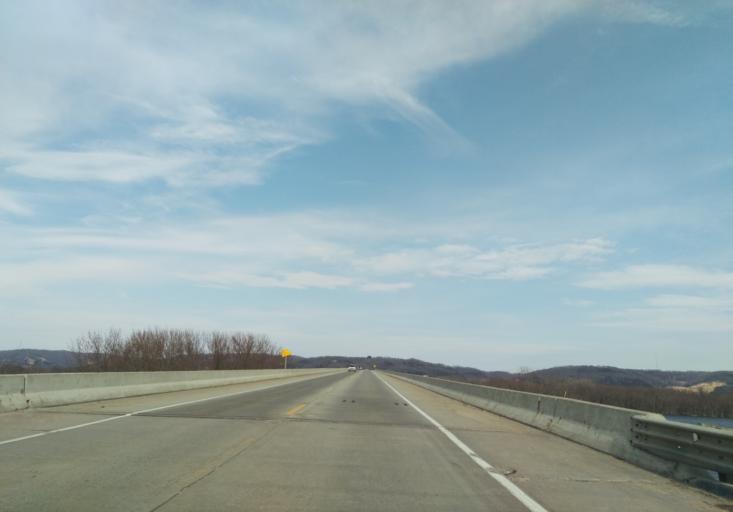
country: US
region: Wisconsin
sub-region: Crawford County
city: Prairie du Chien
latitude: 43.0453
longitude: -91.1627
